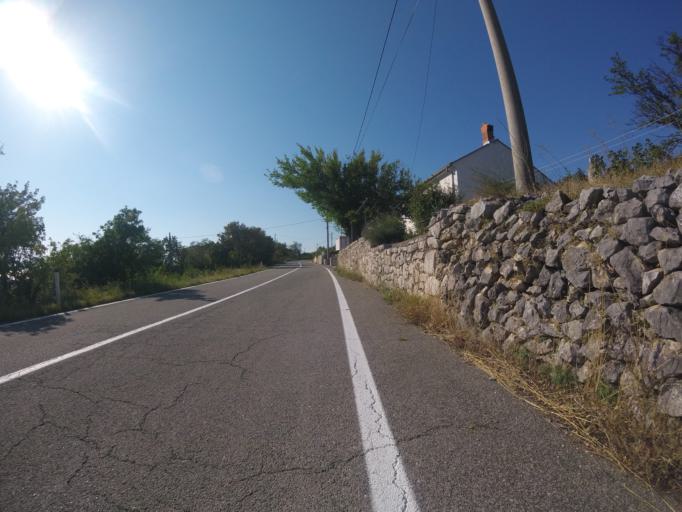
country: HR
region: Primorsko-Goranska
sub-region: Grad Crikvenica
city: Jadranovo
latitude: 45.2467
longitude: 14.6105
